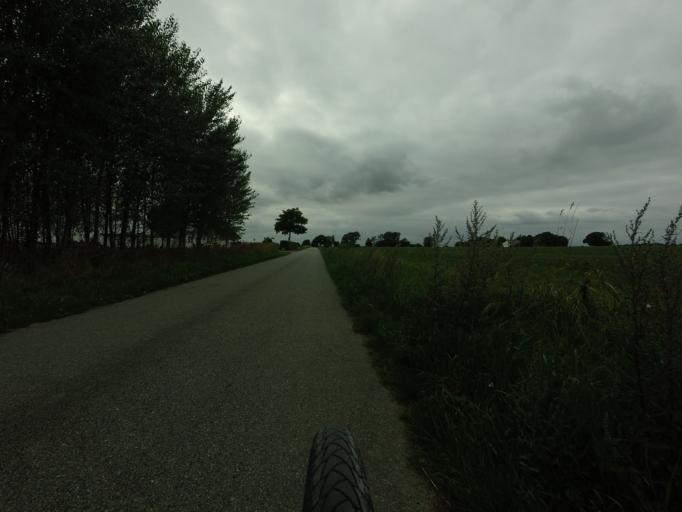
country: DK
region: Zealand
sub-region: Stevns Kommune
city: Store Heddinge
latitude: 55.3372
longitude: 12.4388
